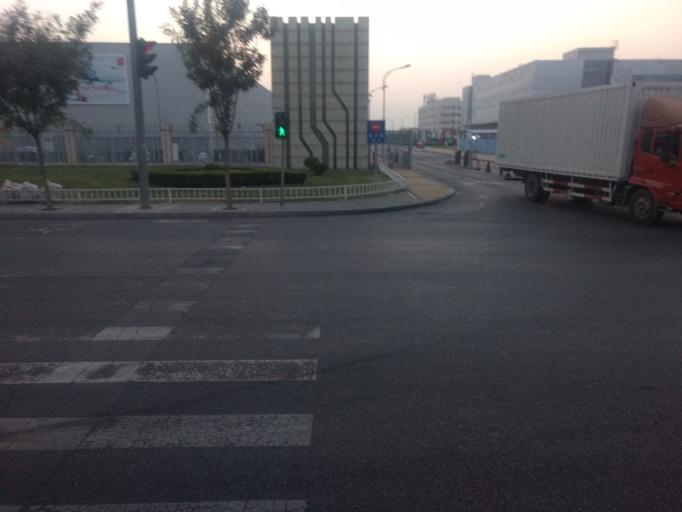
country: CN
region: Beijing
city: Nanfaxin
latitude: 40.0947
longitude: 116.5816
